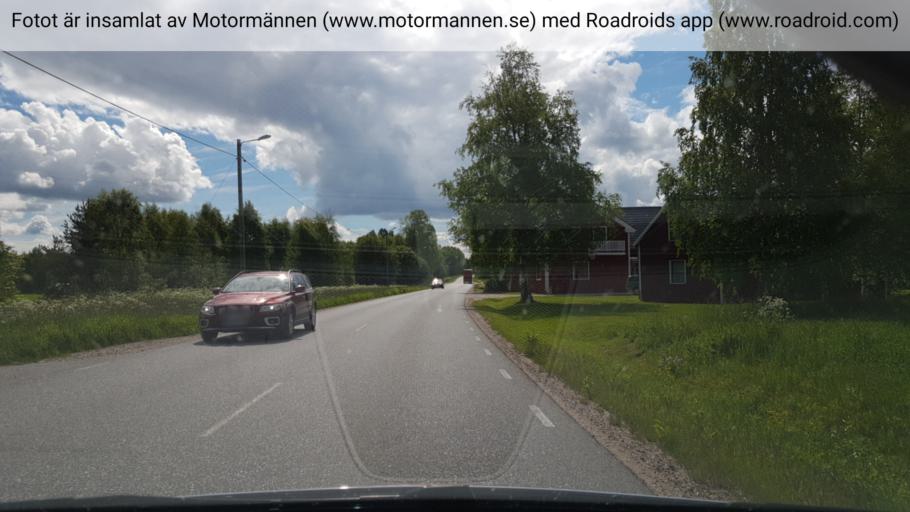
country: FI
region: Lapland
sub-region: Torniolaakso
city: Ylitornio
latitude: 66.2798
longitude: 23.6510
